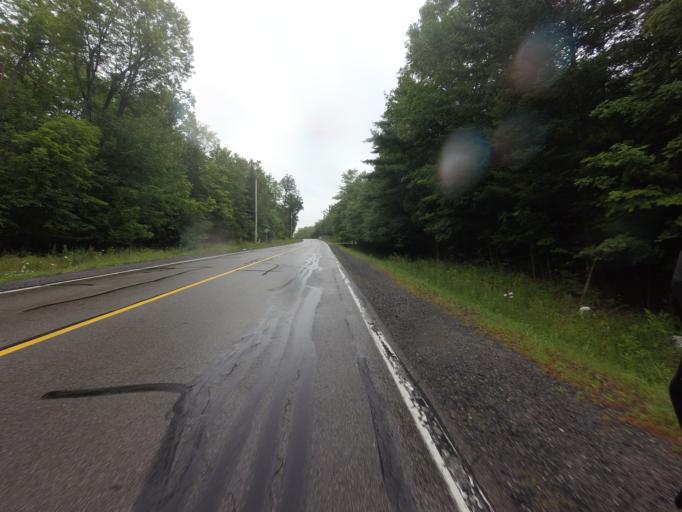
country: CA
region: Ontario
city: Perth
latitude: 44.9852
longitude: -76.3964
